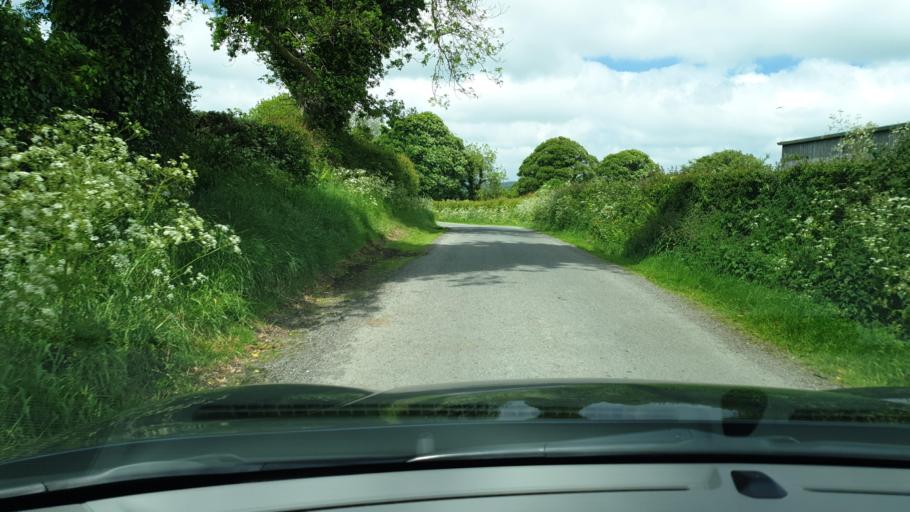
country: IE
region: Leinster
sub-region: An Mhi
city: Slane
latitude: 53.7378
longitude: -6.5606
